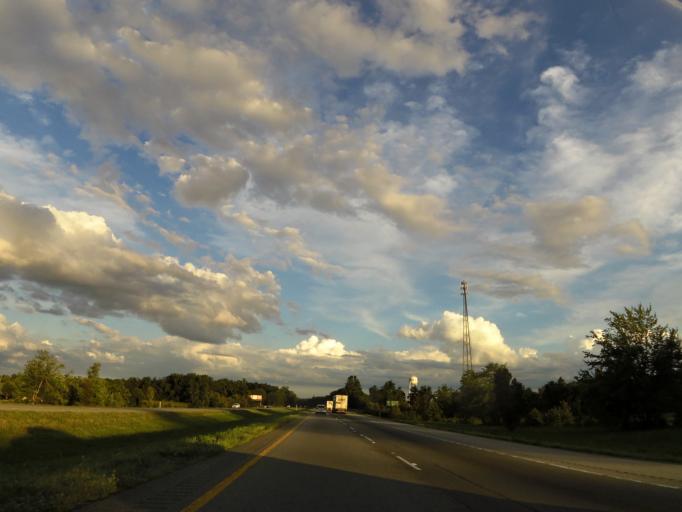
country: US
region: Tennessee
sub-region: Putnam County
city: Monterey
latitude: 36.0977
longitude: -85.2355
